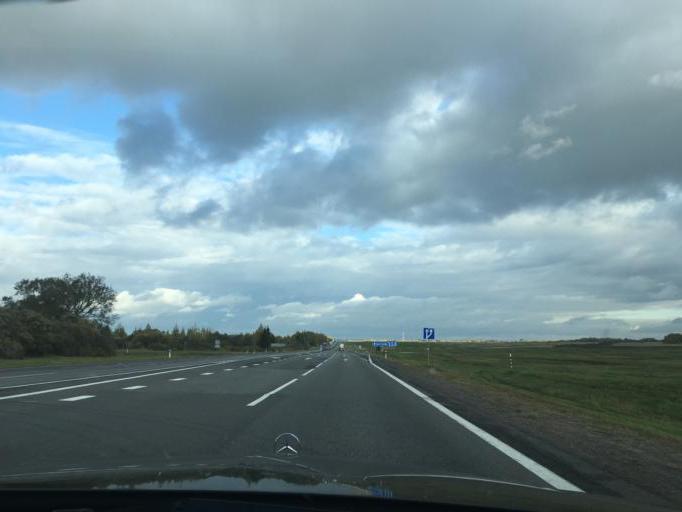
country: BY
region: Vitebsk
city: Dubrowna
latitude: 54.6447
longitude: 30.6014
